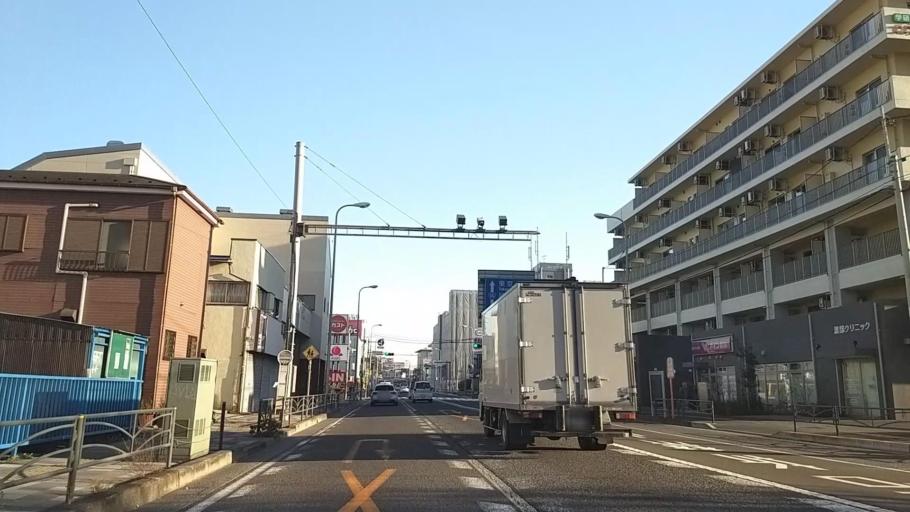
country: JP
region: Kanagawa
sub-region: Kawasaki-shi
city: Kawasaki
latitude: 35.5094
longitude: 139.6824
